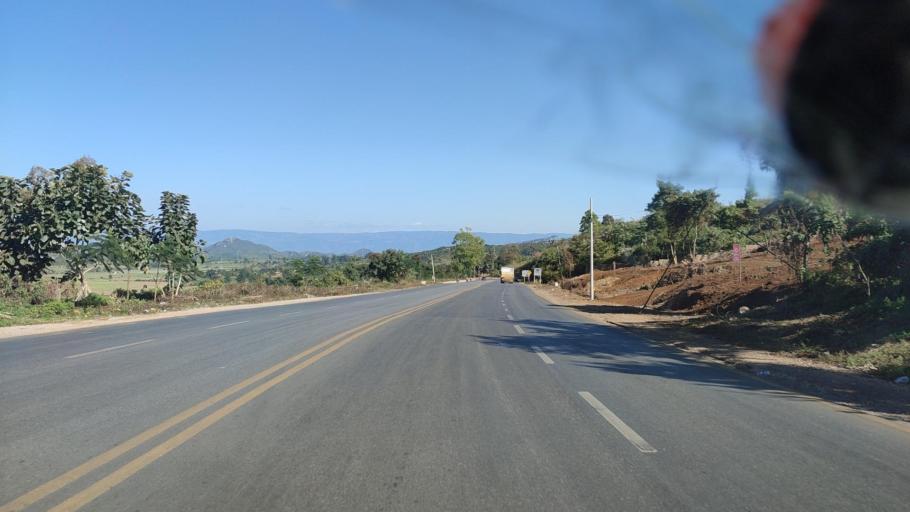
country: MM
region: Mandalay
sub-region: Pyin Oo Lwin District
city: Pyin Oo Lwin
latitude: 22.0772
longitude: 96.5780
